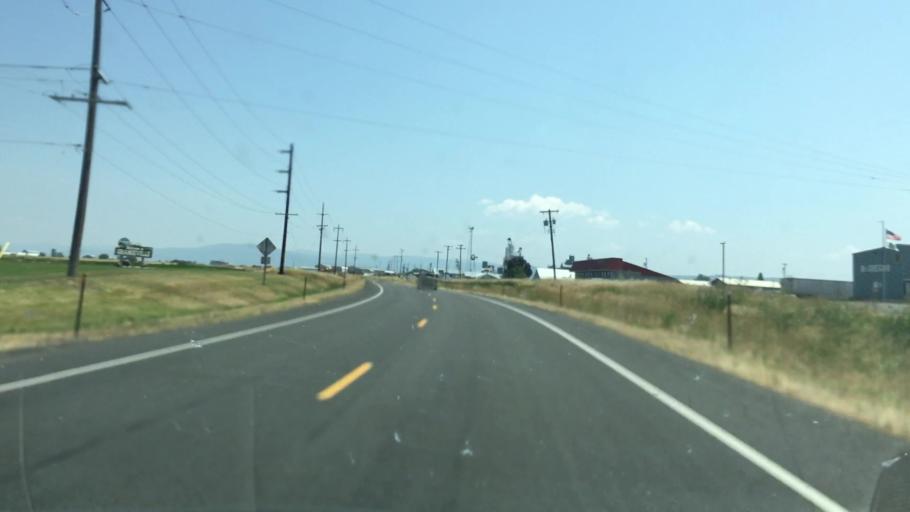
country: US
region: Idaho
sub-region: Idaho County
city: Grangeville
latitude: 45.9358
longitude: -116.1414
